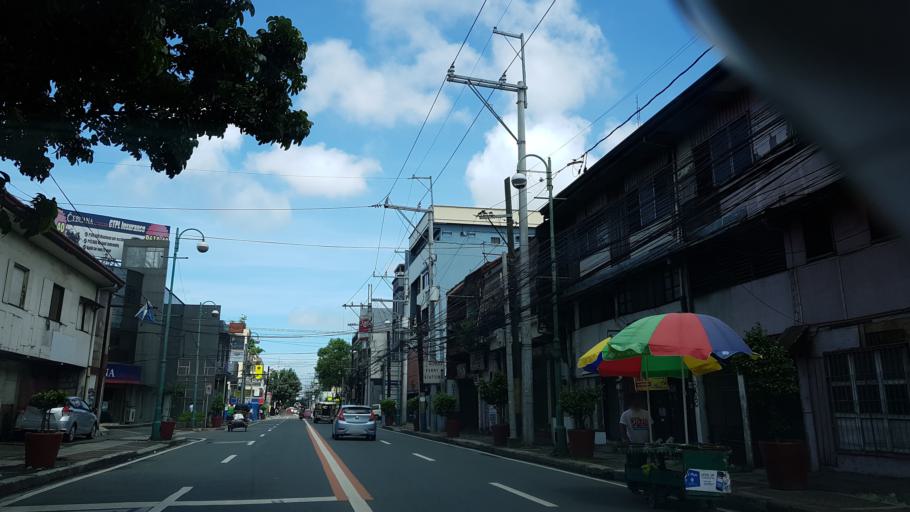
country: PH
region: Metro Manila
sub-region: Makati City
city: Makati City
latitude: 14.5686
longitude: 121.0281
